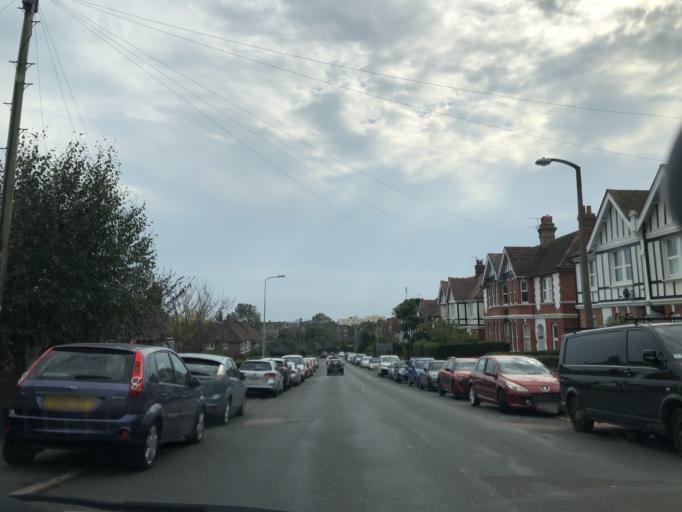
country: GB
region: England
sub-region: East Sussex
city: Bexhill-on-Sea
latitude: 50.8452
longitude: 0.4842
